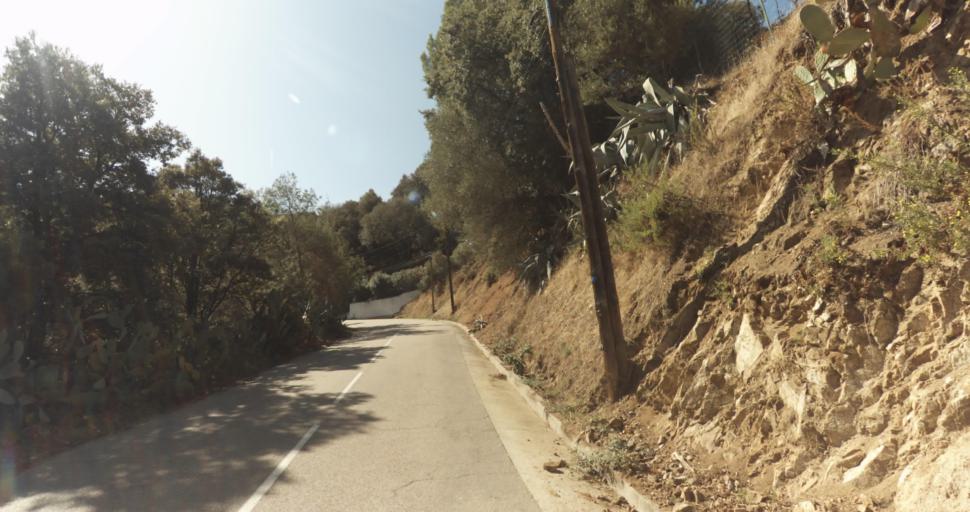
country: FR
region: Corsica
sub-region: Departement de la Corse-du-Sud
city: Ajaccio
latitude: 41.9266
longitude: 8.7081
